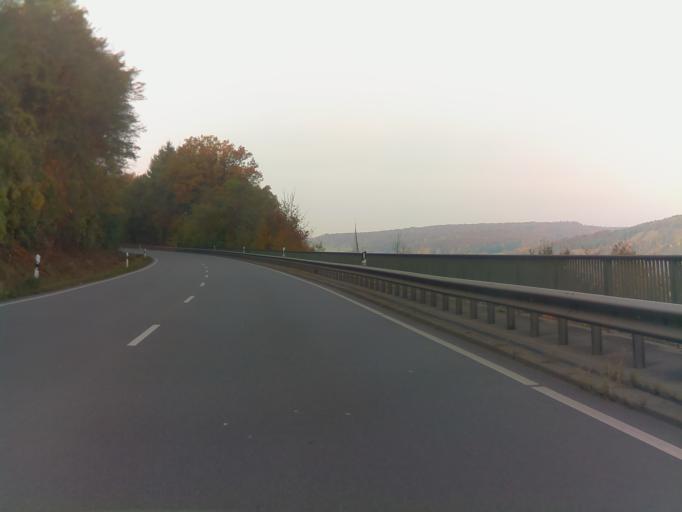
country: DE
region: Baden-Wuerttemberg
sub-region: Karlsruhe Region
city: Obrigheim
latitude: 49.3453
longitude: 9.0963
